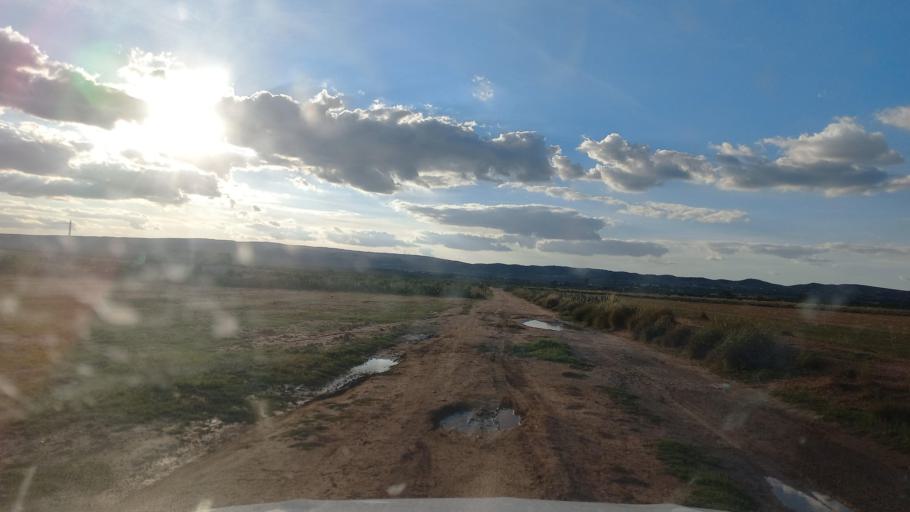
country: TN
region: Al Qasrayn
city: Sbiba
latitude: 35.3511
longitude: 9.0385
